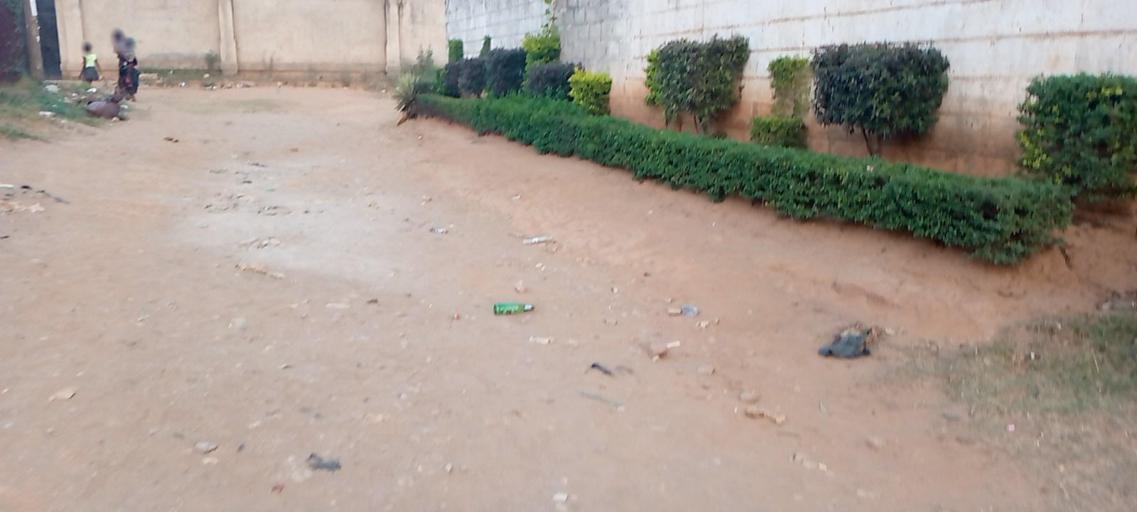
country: ZM
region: Lusaka
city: Lusaka
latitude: -15.4063
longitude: 28.3489
